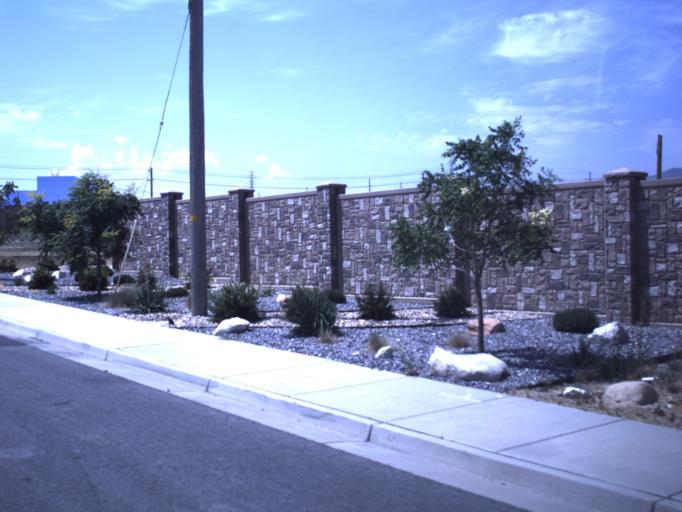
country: US
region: Utah
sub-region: Salt Lake County
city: Kearns
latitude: 40.6691
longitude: -112.0248
